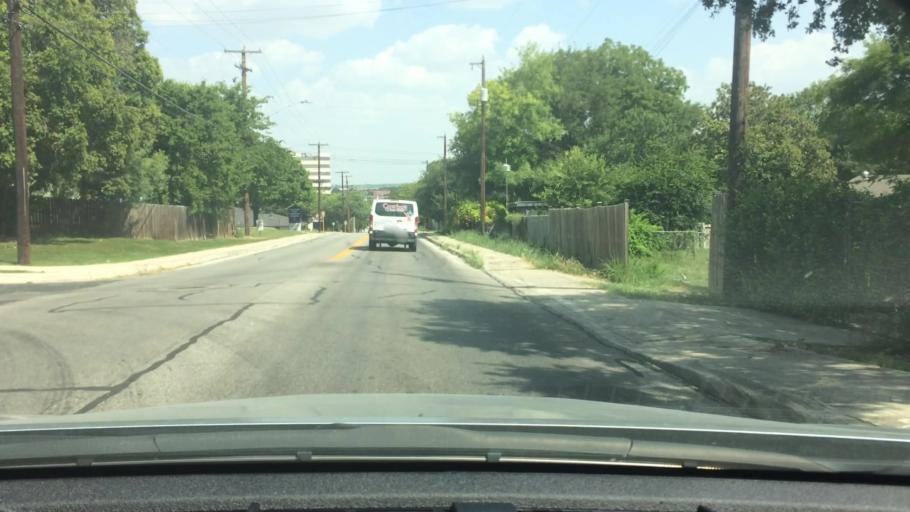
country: US
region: Texas
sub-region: Bexar County
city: Castle Hills
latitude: 29.5335
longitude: -98.4994
